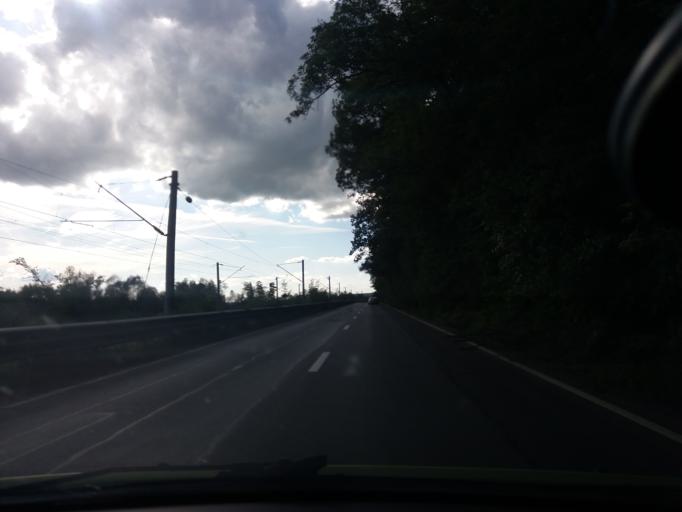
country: RO
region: Arad
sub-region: Comuna Conop
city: Conop
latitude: 46.0993
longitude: 21.8839
